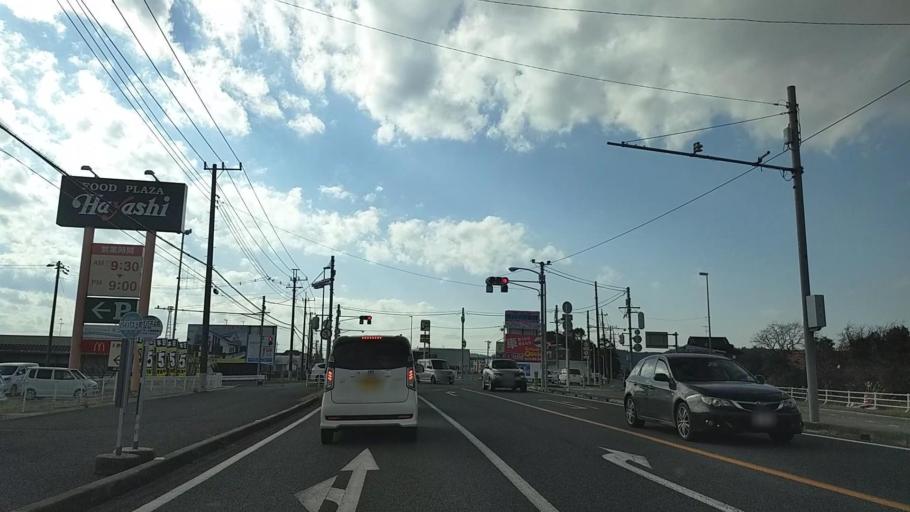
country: JP
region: Chiba
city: Naruto
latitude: 35.6005
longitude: 140.4068
